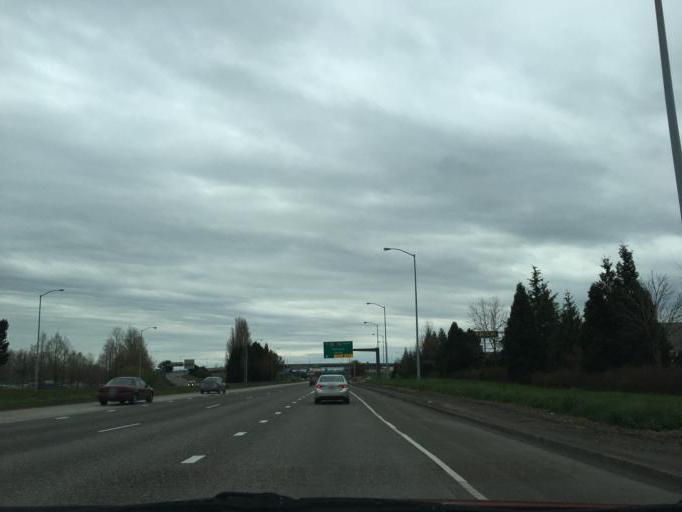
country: US
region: Washington
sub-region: Clark County
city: Mill Plain
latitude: 45.5742
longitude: -122.5557
